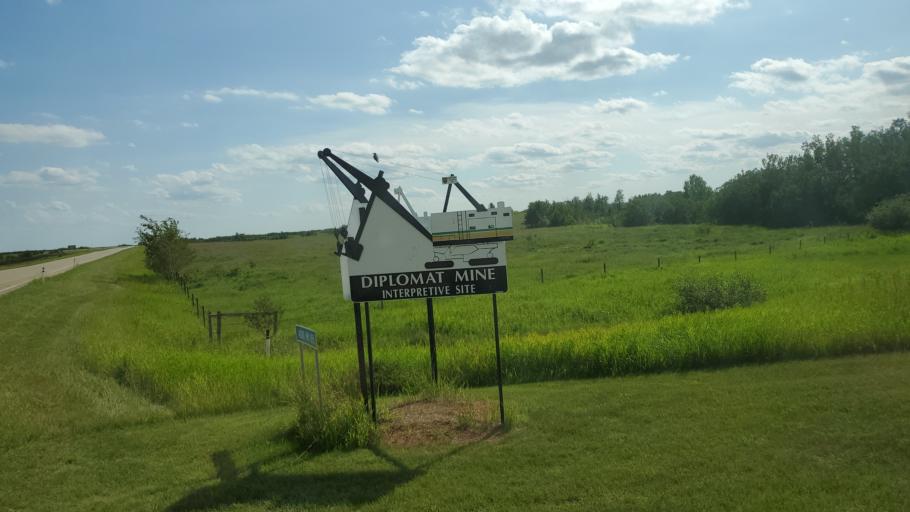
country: CA
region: Alberta
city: Killam
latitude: 52.5064
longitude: -112.1883
